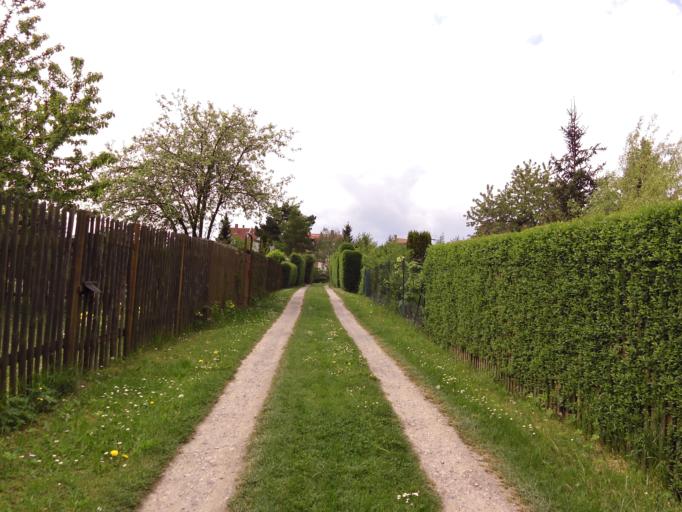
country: DE
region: Thuringia
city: Gotha
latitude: 50.9347
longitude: 10.7003
